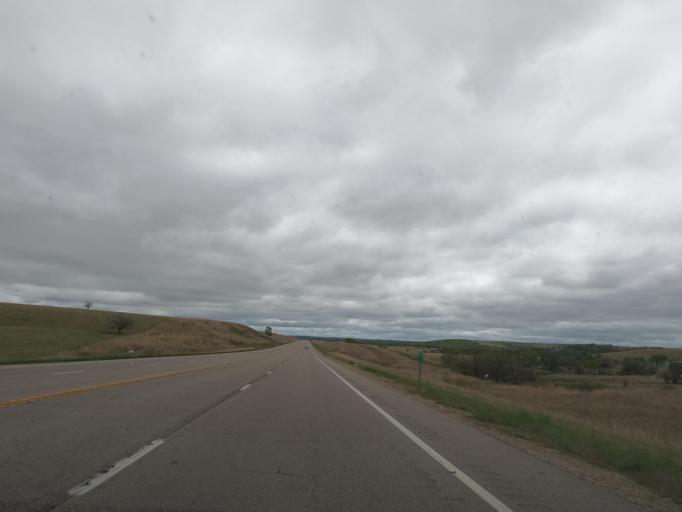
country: US
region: Kansas
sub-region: Greenwood County
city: Eureka
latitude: 37.6429
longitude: -96.4188
